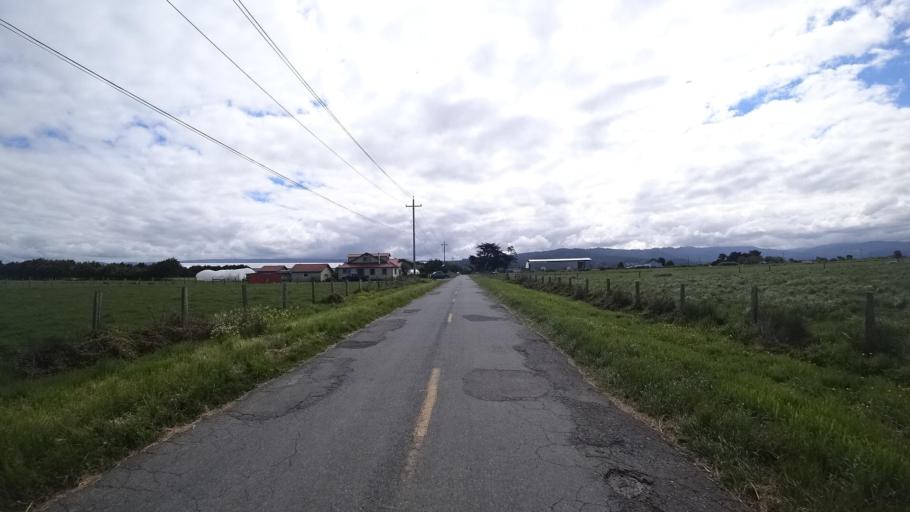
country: US
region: California
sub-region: Humboldt County
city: Arcata
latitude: 40.8831
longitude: -124.1120
